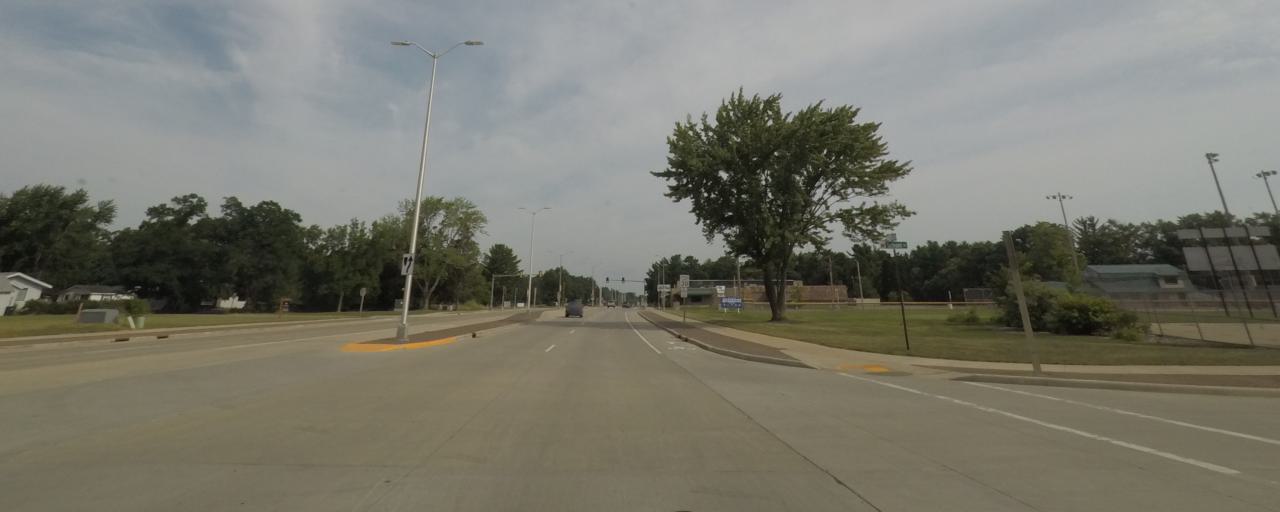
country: US
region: Wisconsin
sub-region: Portage County
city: Plover
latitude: 44.4632
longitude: -89.5441
